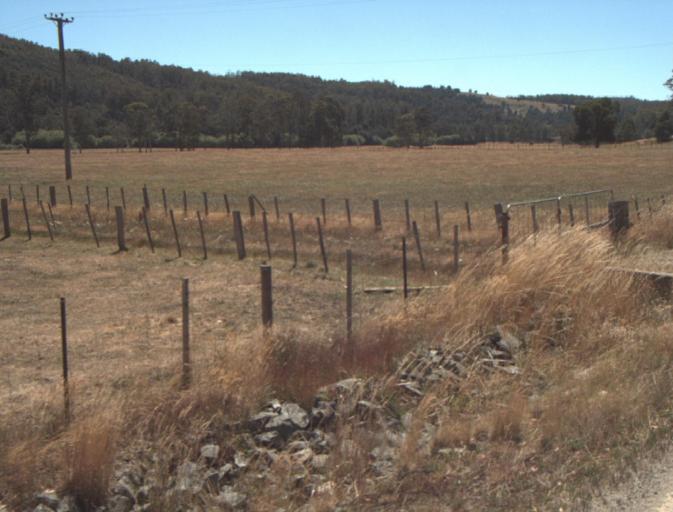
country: AU
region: Tasmania
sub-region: Launceston
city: Newstead
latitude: -41.3237
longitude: 147.3611
